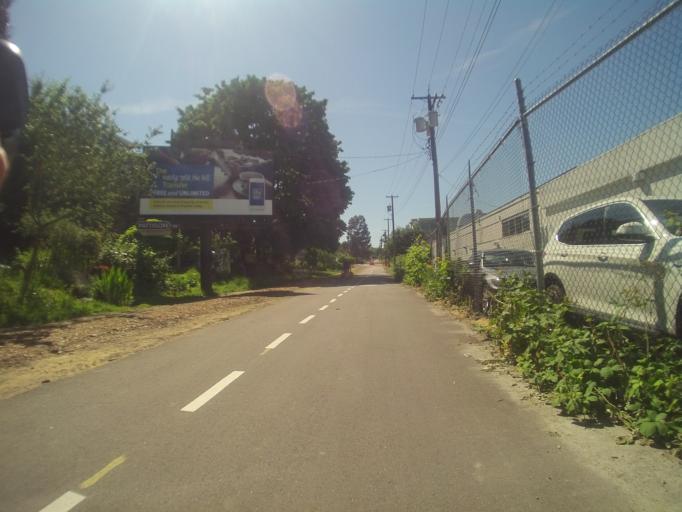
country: CA
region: British Columbia
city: West End
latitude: 49.2664
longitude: -123.1434
